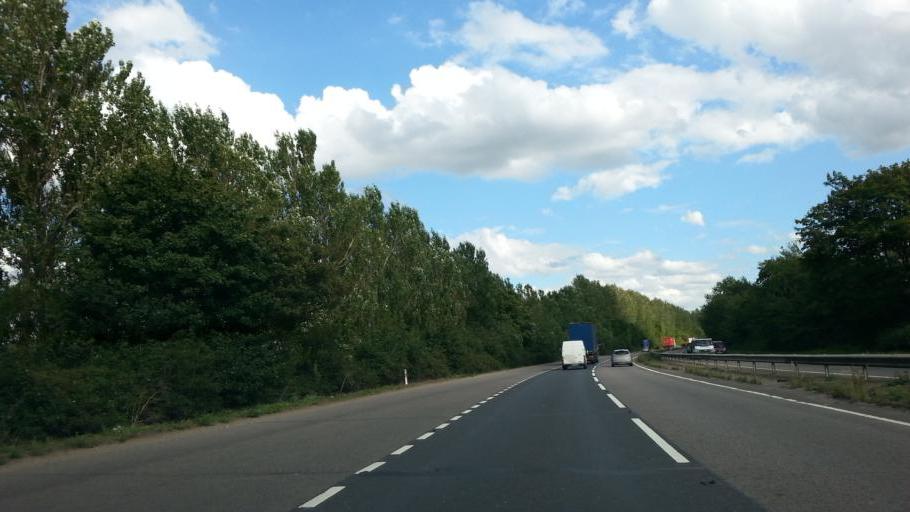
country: GB
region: England
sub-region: Suffolk
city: Thurston
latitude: 52.2379
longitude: 0.8329
